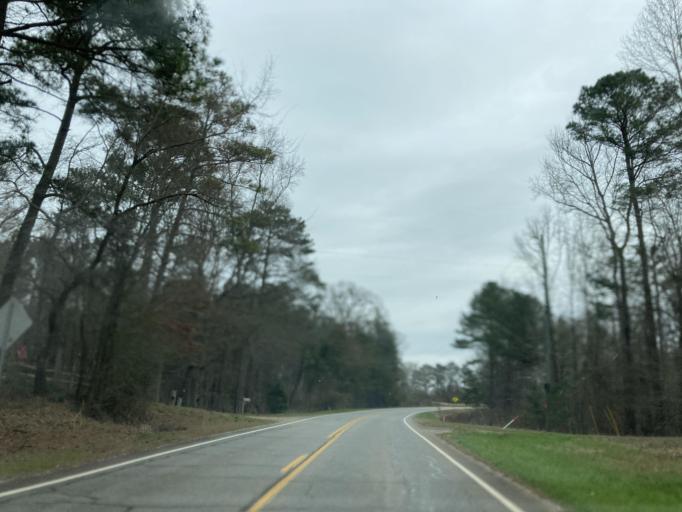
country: US
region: Georgia
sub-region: Jones County
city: Gray
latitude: 32.9733
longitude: -83.6277
